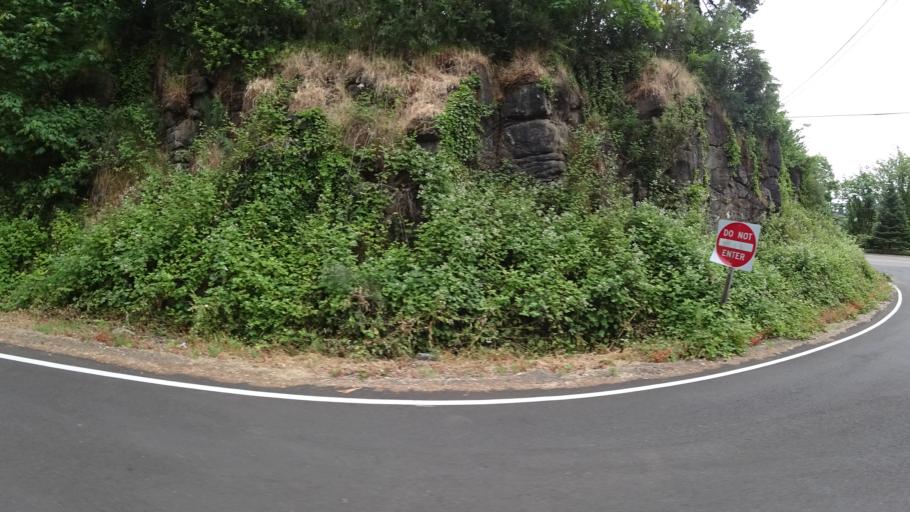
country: US
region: Oregon
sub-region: Clackamas County
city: Lake Oswego
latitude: 45.4246
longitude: -122.6610
